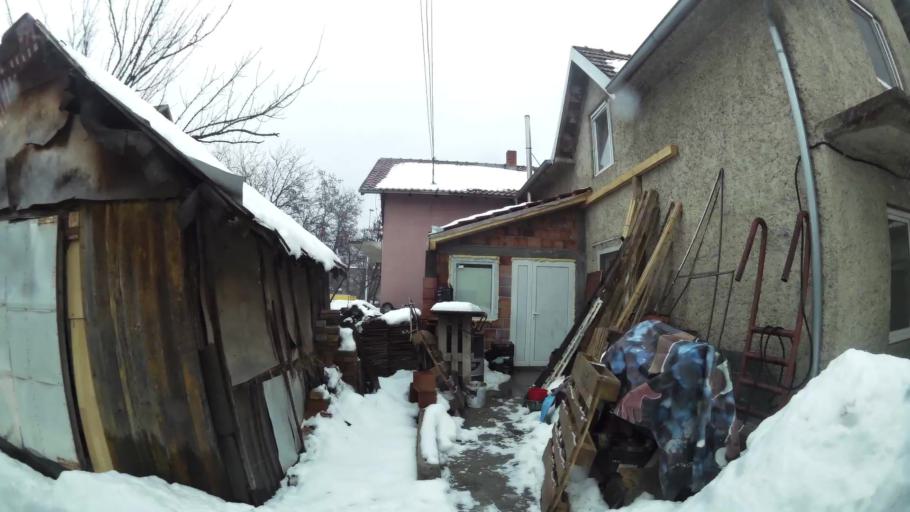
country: RS
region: Central Serbia
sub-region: Belgrade
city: Zemun
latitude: 44.8415
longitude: 20.3669
